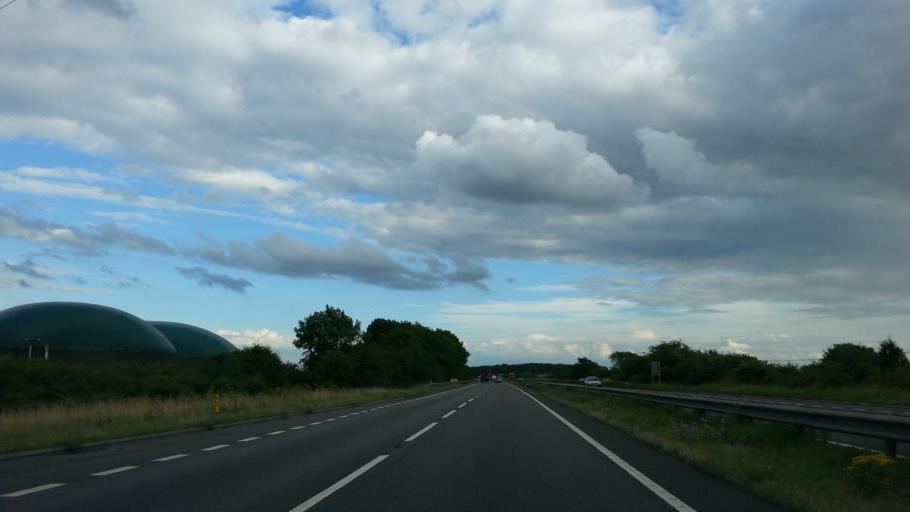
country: GB
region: England
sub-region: Nottinghamshire
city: Tuxford
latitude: 53.2192
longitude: -0.8832
